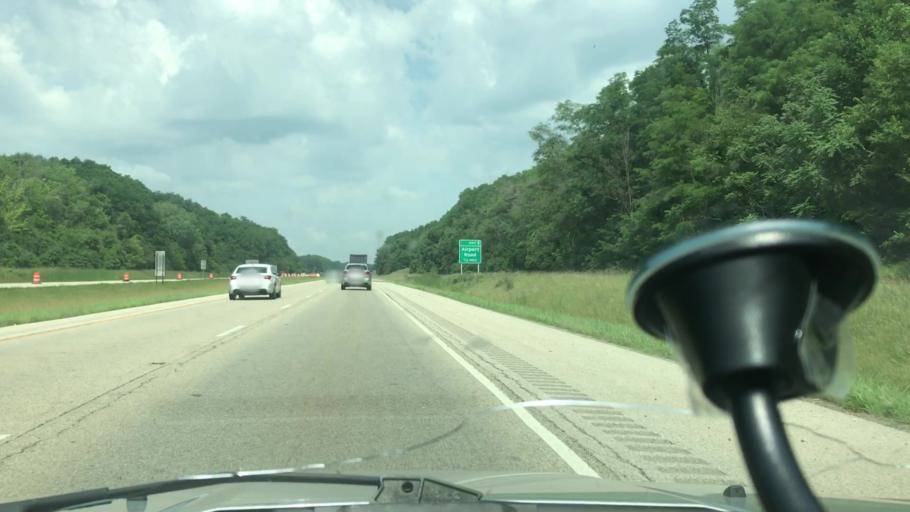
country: US
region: Illinois
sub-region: Peoria County
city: Bartonville
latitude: 40.6656
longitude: -89.6567
